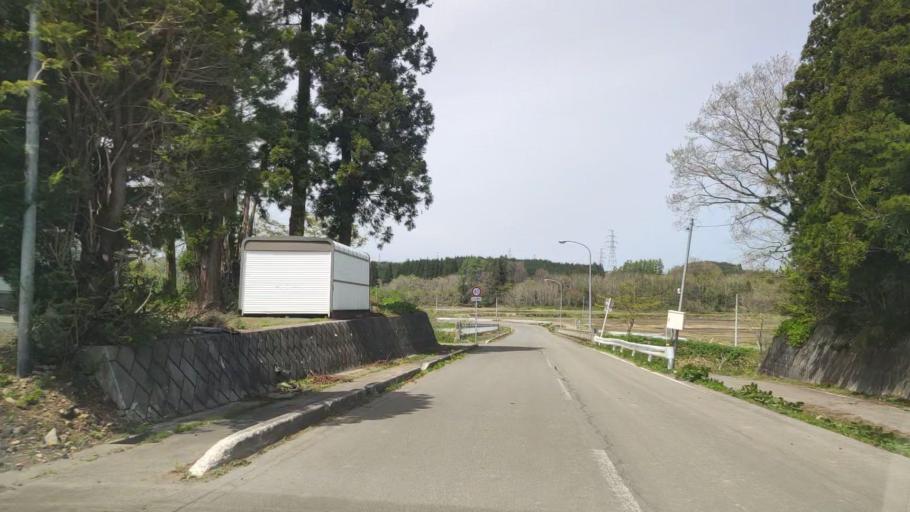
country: JP
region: Aomori
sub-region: Misawa Shi
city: Inuotose
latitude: 40.7807
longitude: 141.1209
